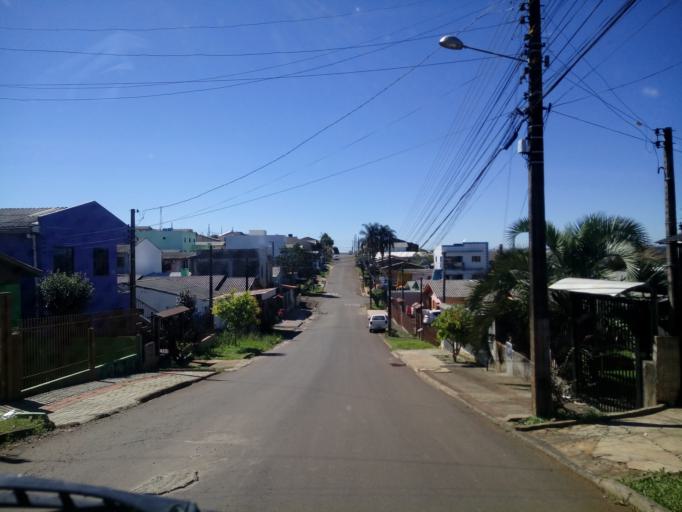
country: BR
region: Santa Catarina
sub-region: Chapeco
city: Chapeco
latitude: -27.0890
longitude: -52.6749
